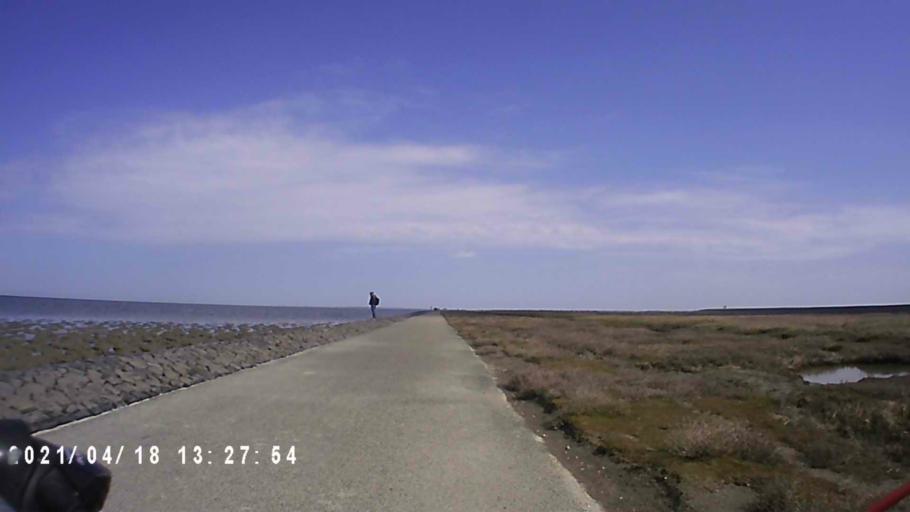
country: NL
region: Friesland
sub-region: Gemeente Dongeradeel
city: Anjum
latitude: 53.4063
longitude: 6.0884
